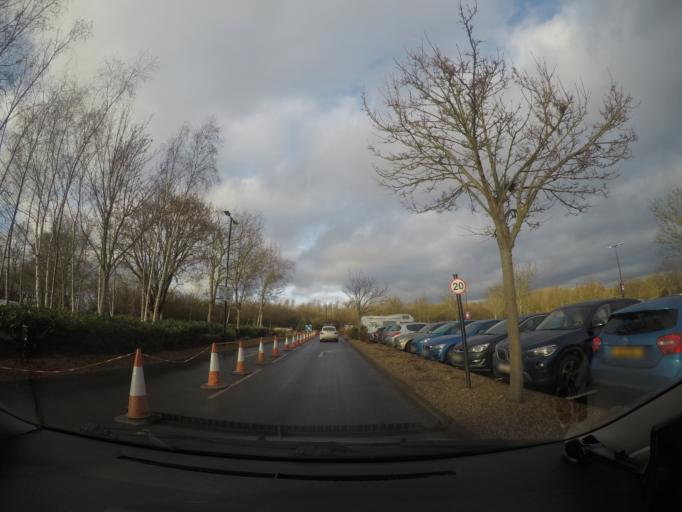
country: GB
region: England
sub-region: City of York
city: Fulford
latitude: 53.9244
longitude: -1.0778
